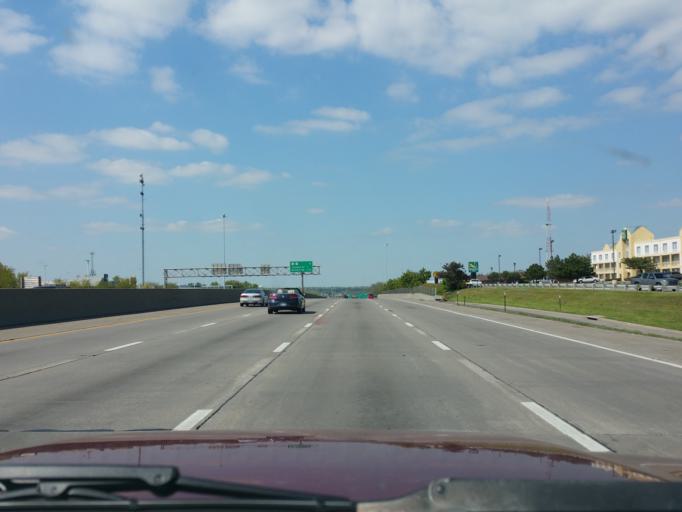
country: US
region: Kansas
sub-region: Johnson County
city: Merriam
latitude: 39.0080
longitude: -94.6937
